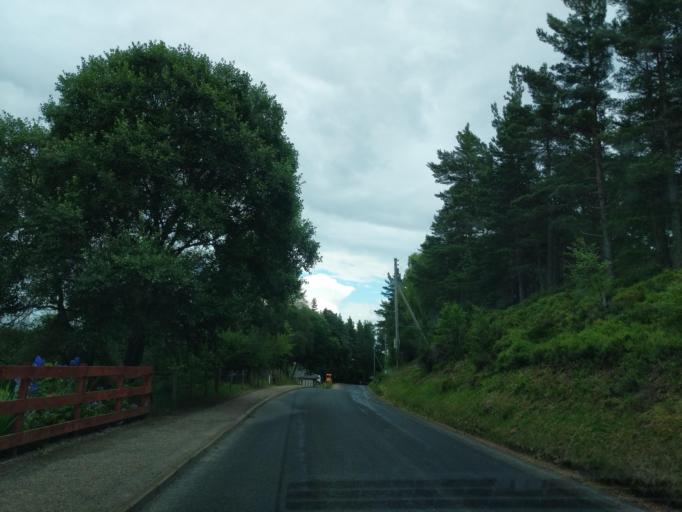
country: GB
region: Scotland
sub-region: Highland
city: Aviemore
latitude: 57.2831
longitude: -3.8241
